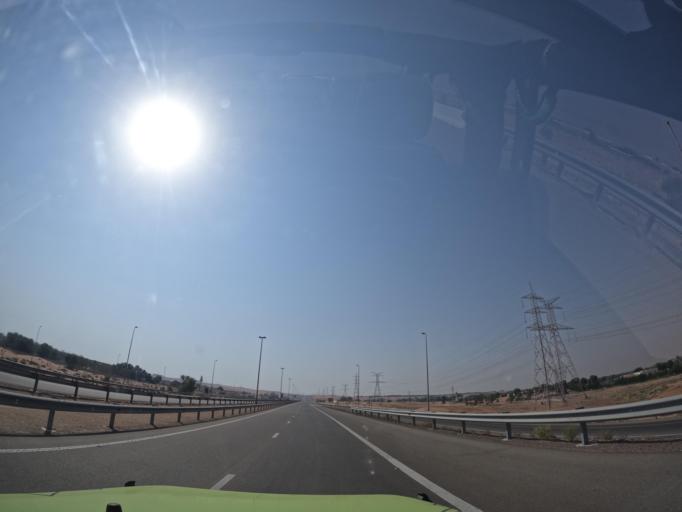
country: OM
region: Al Buraimi
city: Al Buraymi
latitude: 24.3648
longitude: 55.7295
